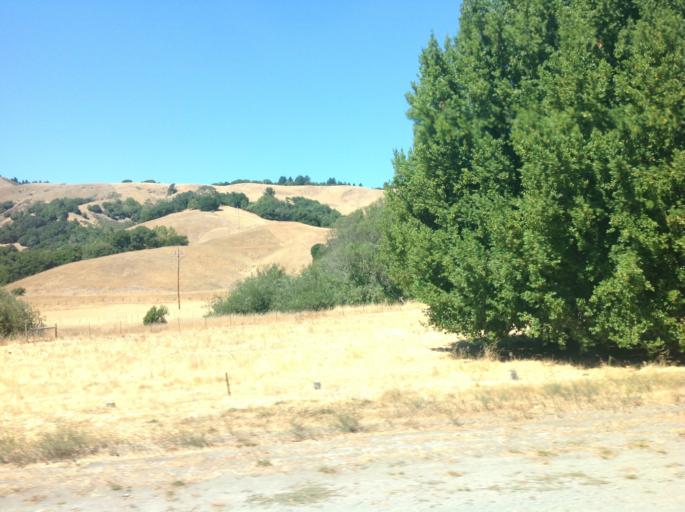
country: US
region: California
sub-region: Marin County
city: Woodacre
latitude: 38.0160
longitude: -122.6383
